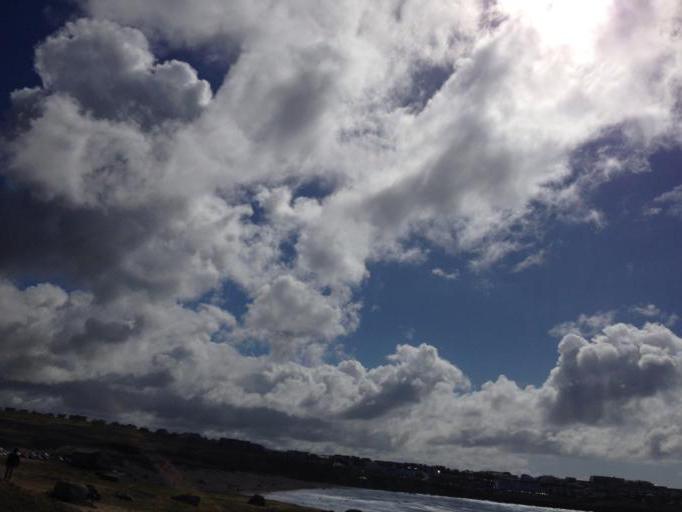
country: GB
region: England
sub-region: Cornwall
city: Newquay
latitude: 50.4209
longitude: -5.0983
